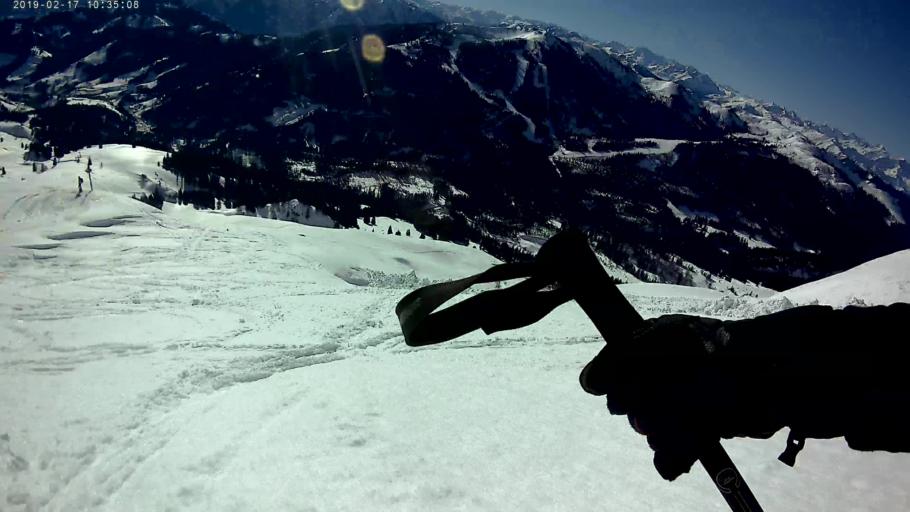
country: AT
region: Salzburg
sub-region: Politischer Bezirk Sankt Johann im Pongau
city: Muhlbach am Hochkonig
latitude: 47.4087
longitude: 13.0802
